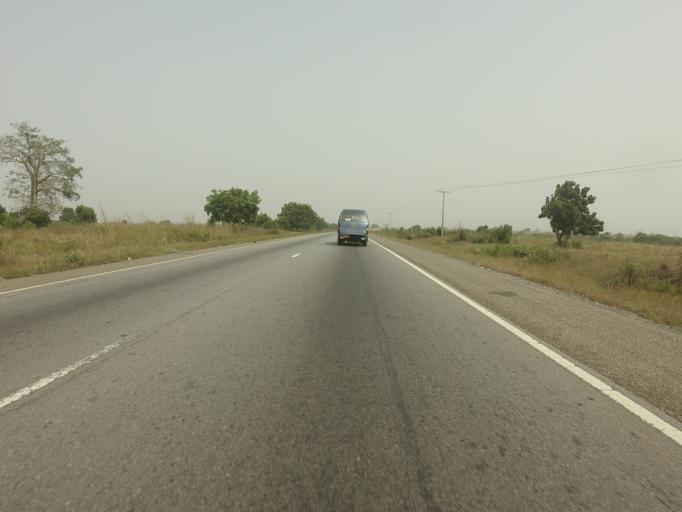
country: GH
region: Volta
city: Anloga
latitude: 5.8860
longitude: 0.4443
